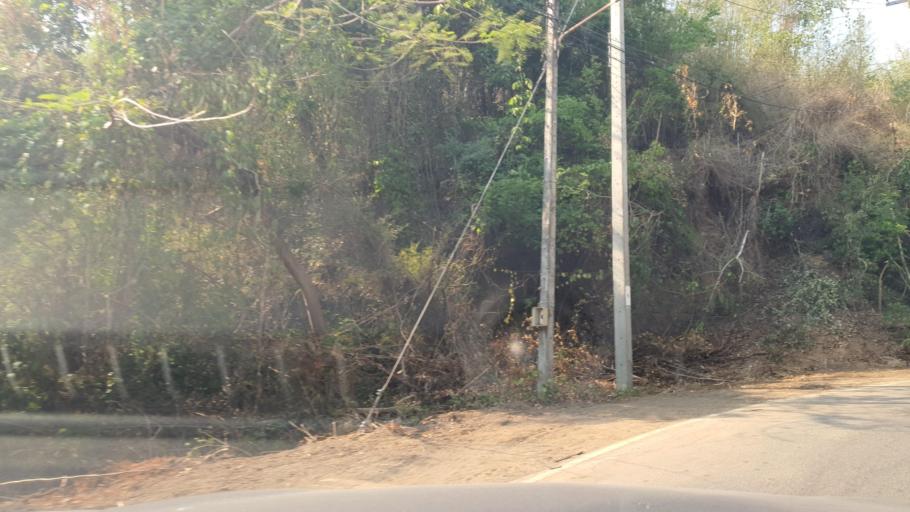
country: TH
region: Kanchanaburi
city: Si Sawat
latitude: 14.3787
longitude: 99.1408
